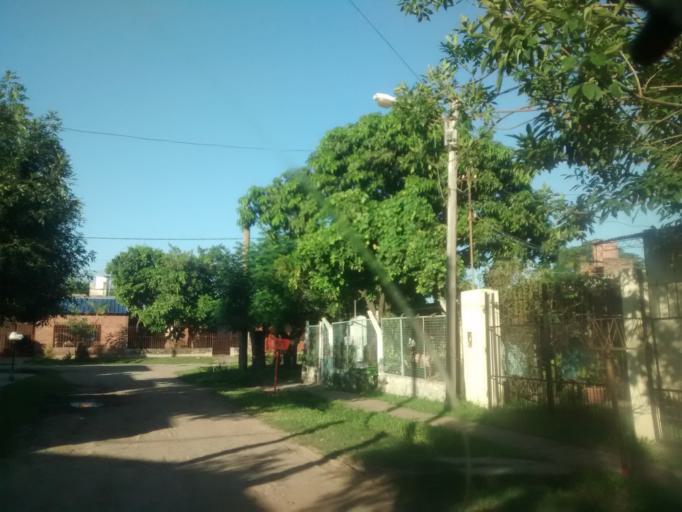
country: AR
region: Chaco
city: Fontana
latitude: -27.4493
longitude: -59.0237
